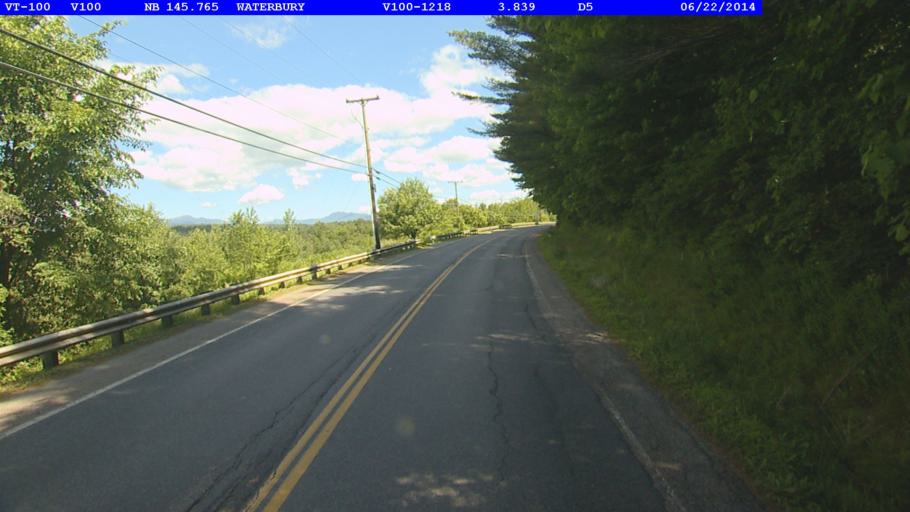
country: US
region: Vermont
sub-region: Washington County
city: Waterbury
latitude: 44.3845
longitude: -72.7207
